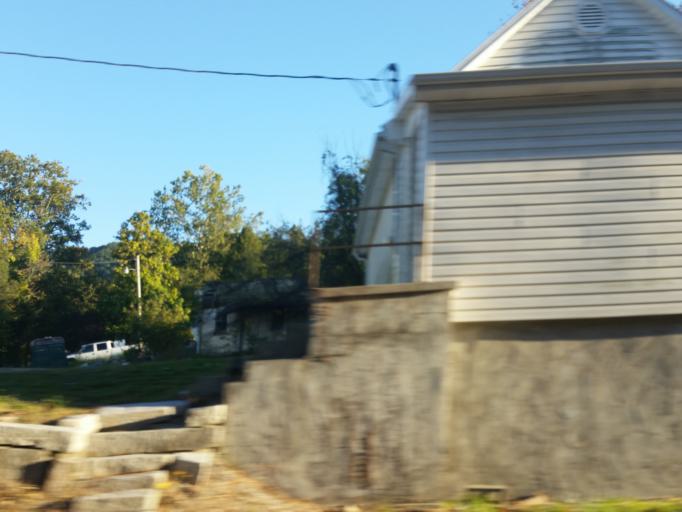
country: US
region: Tennessee
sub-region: Grainger County
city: Rutledge
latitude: 36.3147
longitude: -83.5397
